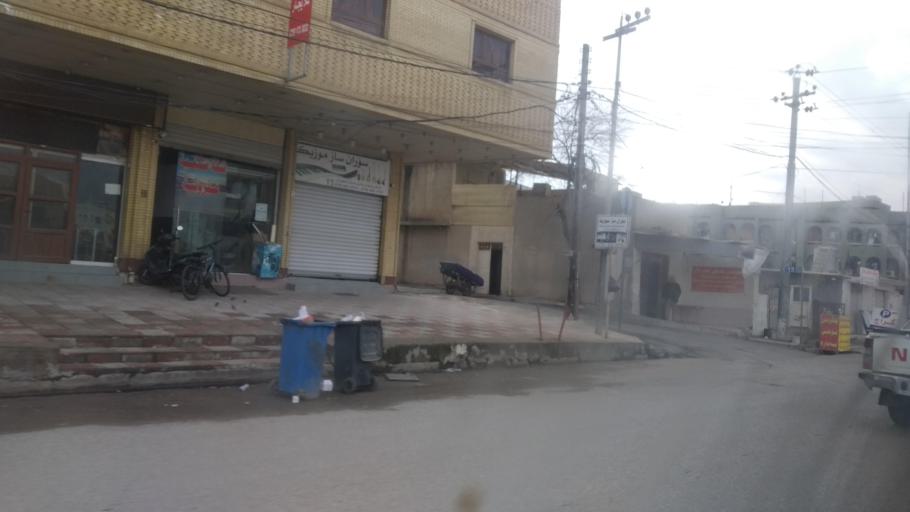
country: IQ
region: Arbil
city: Erbil
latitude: 36.1945
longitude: 44.0141
